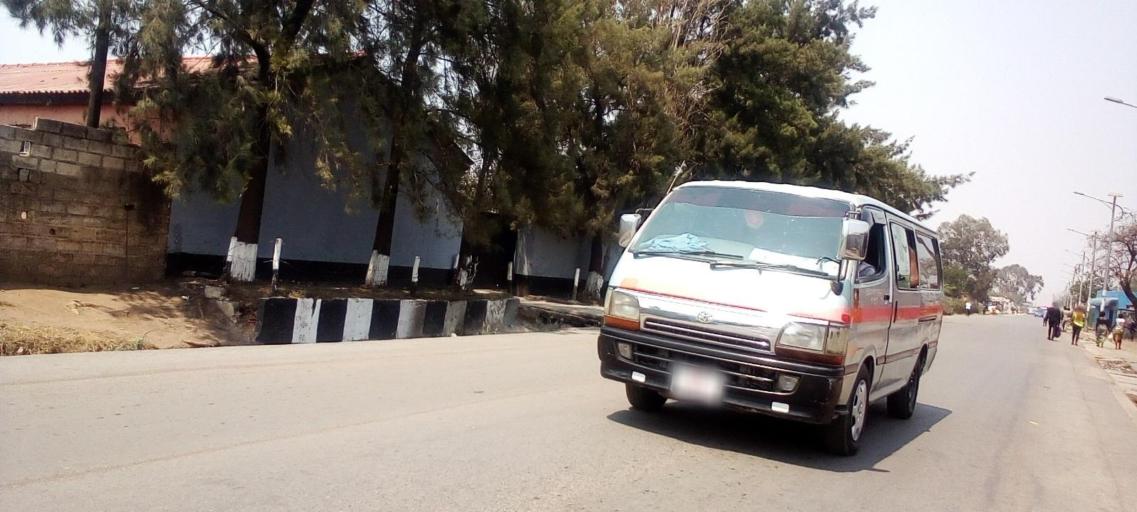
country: ZM
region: Lusaka
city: Lusaka
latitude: -15.4378
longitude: 28.2563
